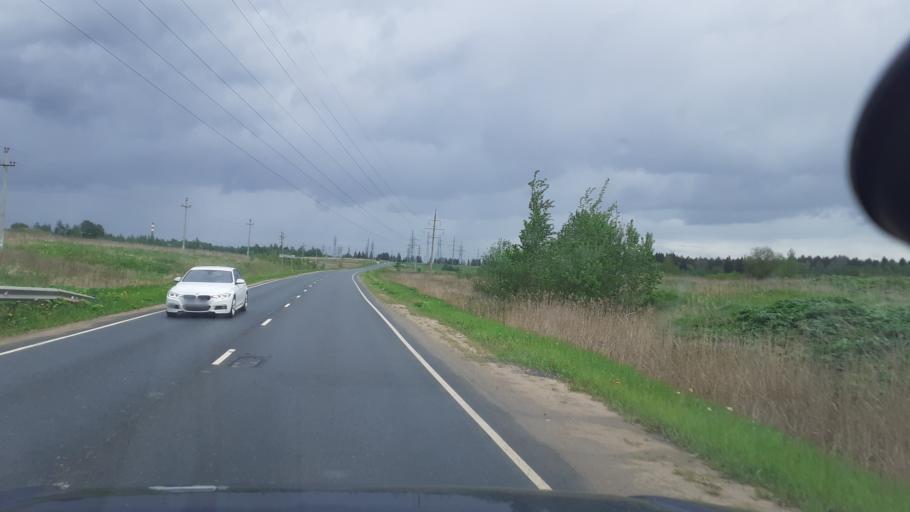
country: RU
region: Moskovskaya
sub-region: Volokolamskiy Rayon
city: Volokolamsk
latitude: 56.0202
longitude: 35.9462
